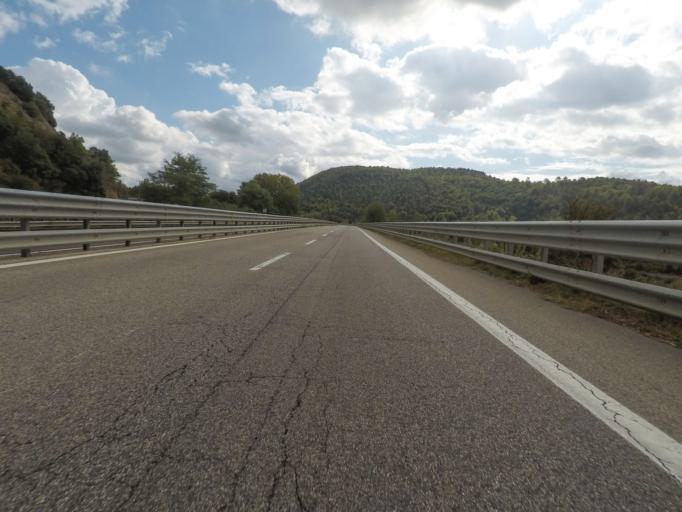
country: IT
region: Tuscany
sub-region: Provincia di Siena
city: Rapolano Terme
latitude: 43.2918
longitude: 11.6106
